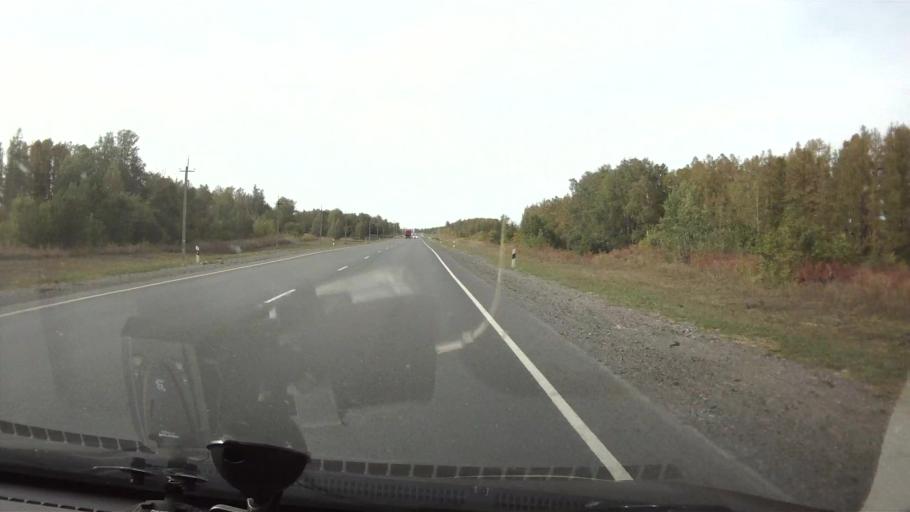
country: RU
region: Saratov
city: Shikhany
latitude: 52.1534
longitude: 47.1840
